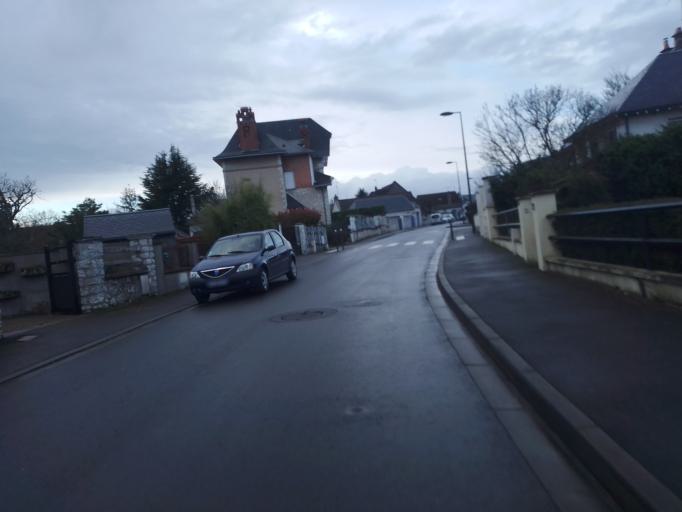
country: FR
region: Centre
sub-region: Departement du Loir-et-Cher
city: Blois
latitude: 47.5977
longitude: 1.3459
